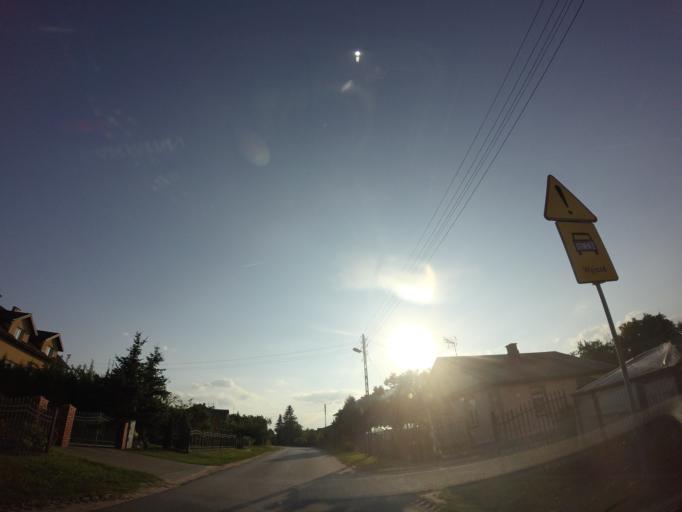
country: PL
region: Lublin Voivodeship
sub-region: Powiat pulawski
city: Kurow
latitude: 51.4156
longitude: 22.2242
